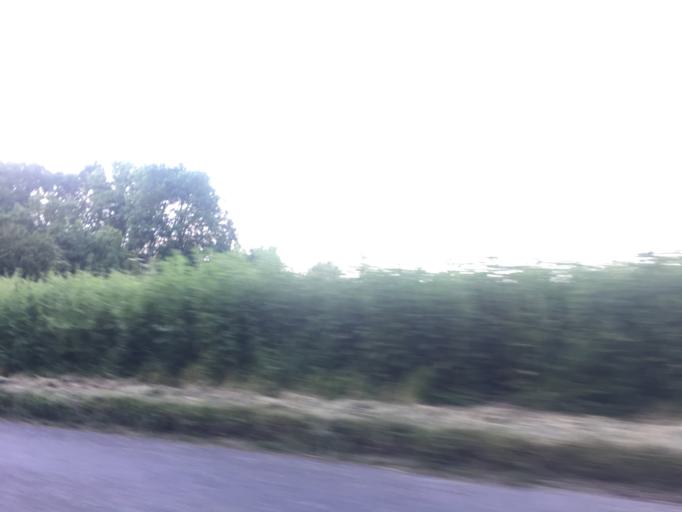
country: GB
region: England
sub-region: Leicestershire
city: Great Glen
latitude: 52.6125
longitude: -1.0434
